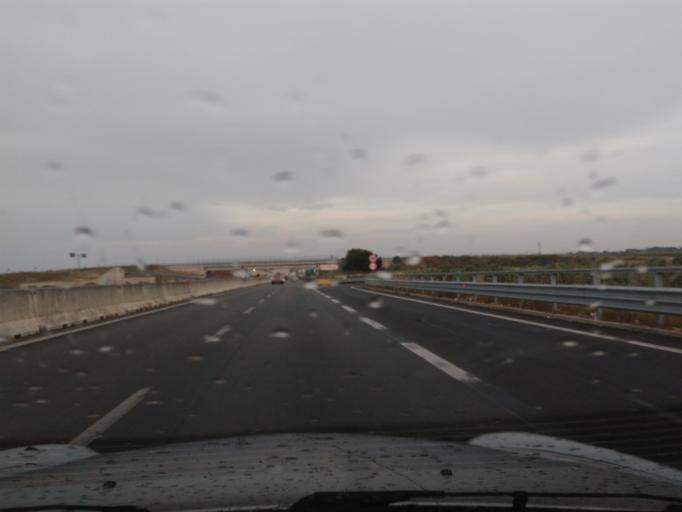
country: IT
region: Apulia
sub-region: Provincia di Bari
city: Molfetta
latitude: 41.2032
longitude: 16.5694
